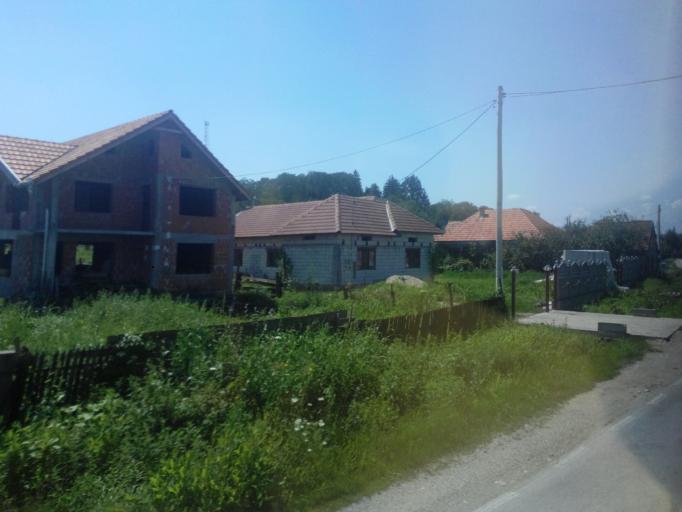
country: RO
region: Hunedoara
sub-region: Comuna Dobra
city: Dobra
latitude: 45.9171
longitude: 22.5607
